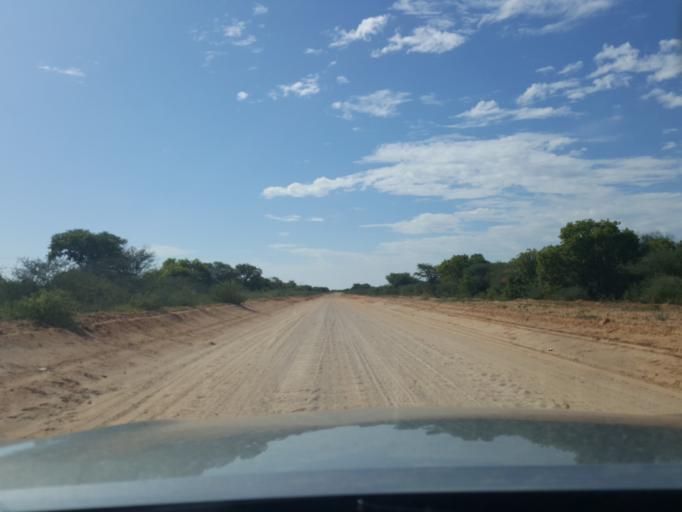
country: BW
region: Kweneng
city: Khudumelapye
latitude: -23.7512
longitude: 24.7553
